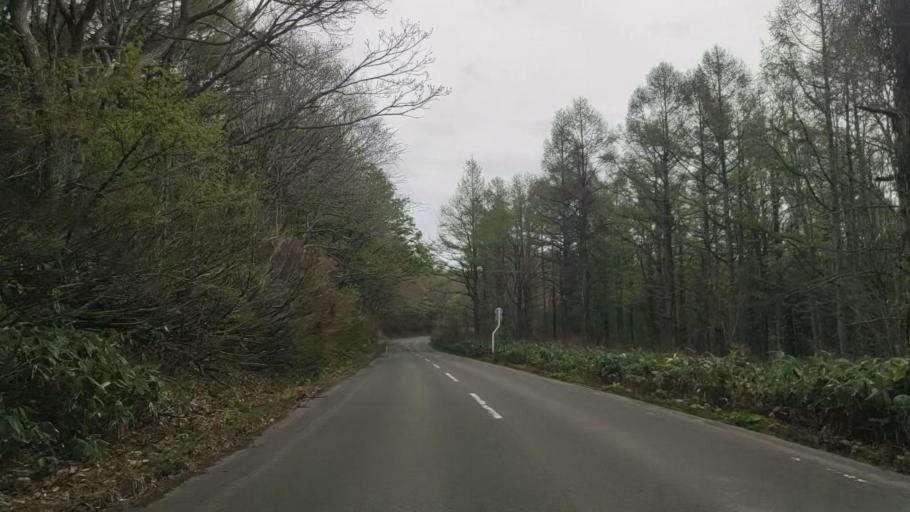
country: JP
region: Aomori
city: Aomori Shi
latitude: 40.7314
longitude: 140.8418
